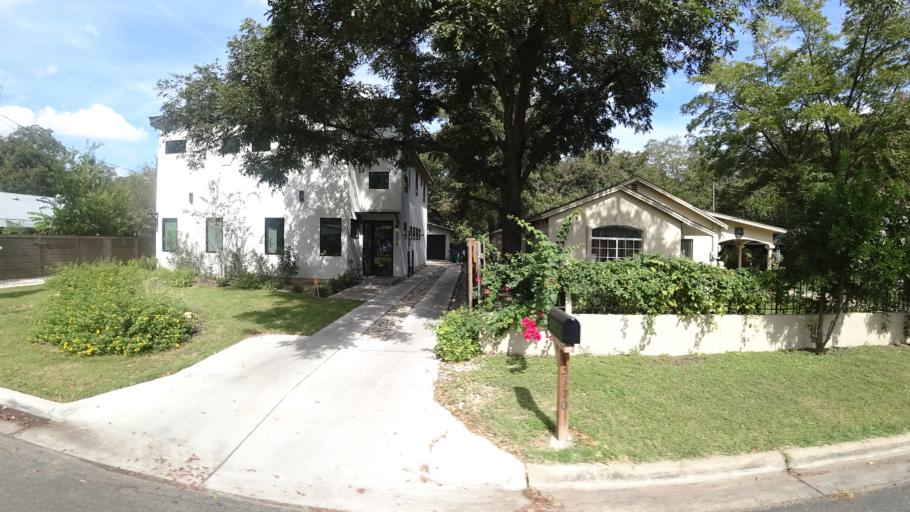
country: US
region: Texas
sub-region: Travis County
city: Austin
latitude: 30.2647
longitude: -97.7014
